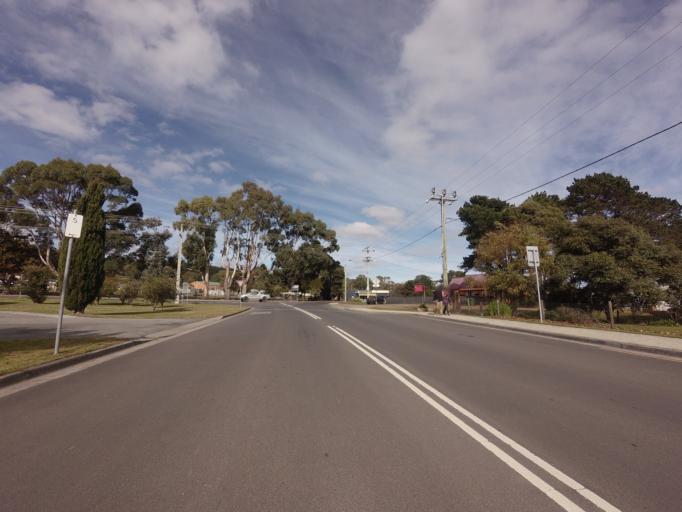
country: AU
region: Tasmania
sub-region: Clarence
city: Sandford
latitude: -43.0973
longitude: 147.7437
